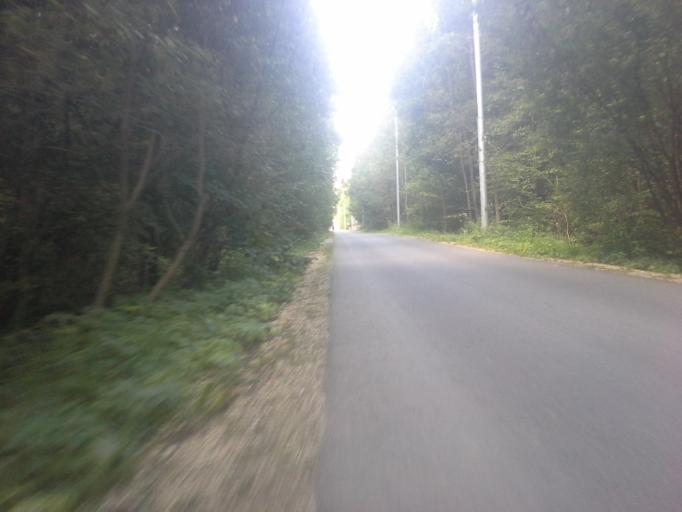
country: RU
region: Moskovskaya
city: Kievskij
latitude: 55.3432
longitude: 36.9486
